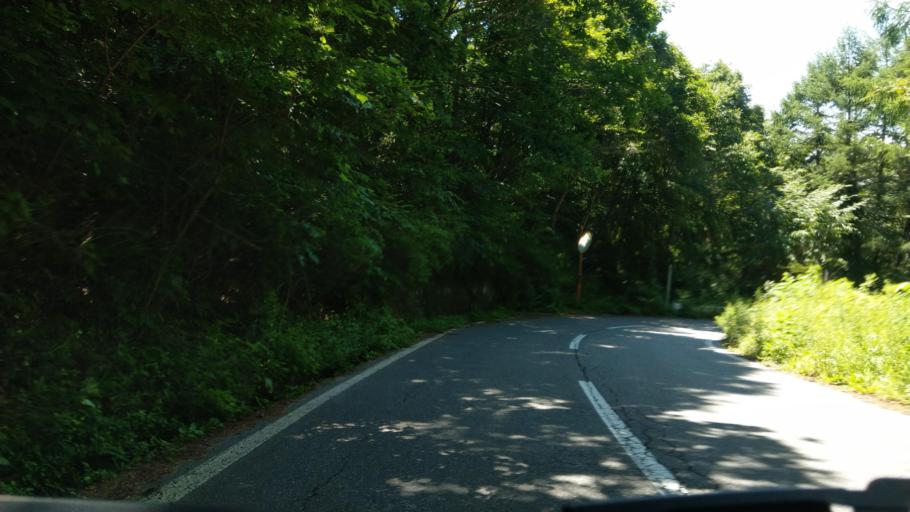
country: JP
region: Nagano
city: Komoro
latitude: 36.3753
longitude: 138.4636
